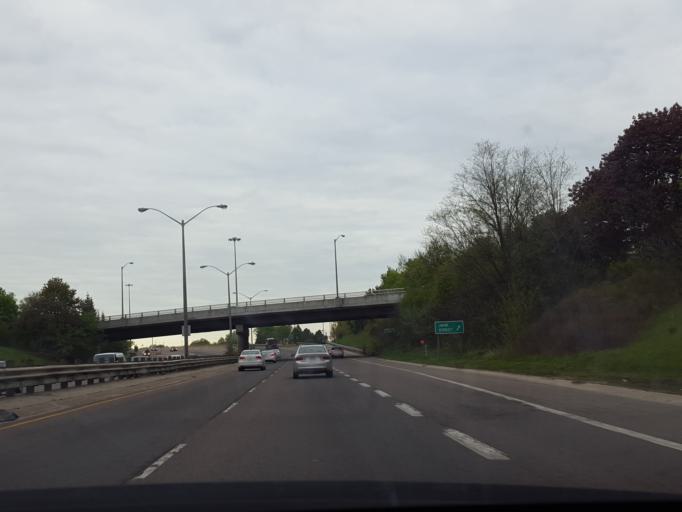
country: CA
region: Ontario
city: Toronto
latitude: 43.7092
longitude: -79.5000
